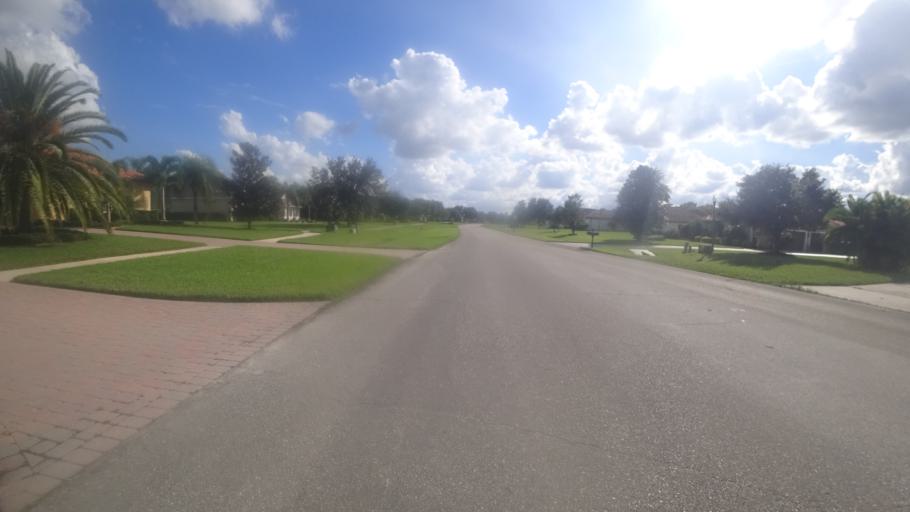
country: US
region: Florida
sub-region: Manatee County
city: Ellenton
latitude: 27.5464
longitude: -82.3916
